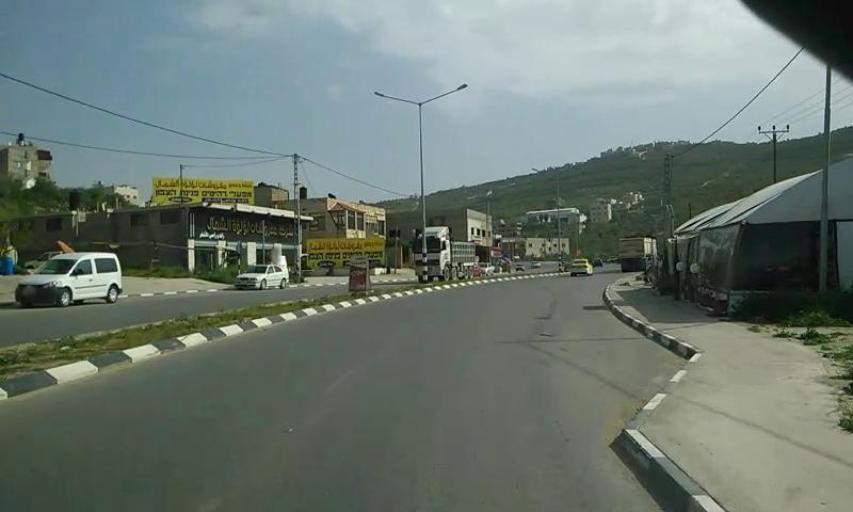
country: PS
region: West Bank
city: Dayr Sharaf
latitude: 32.2538
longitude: 35.1860
